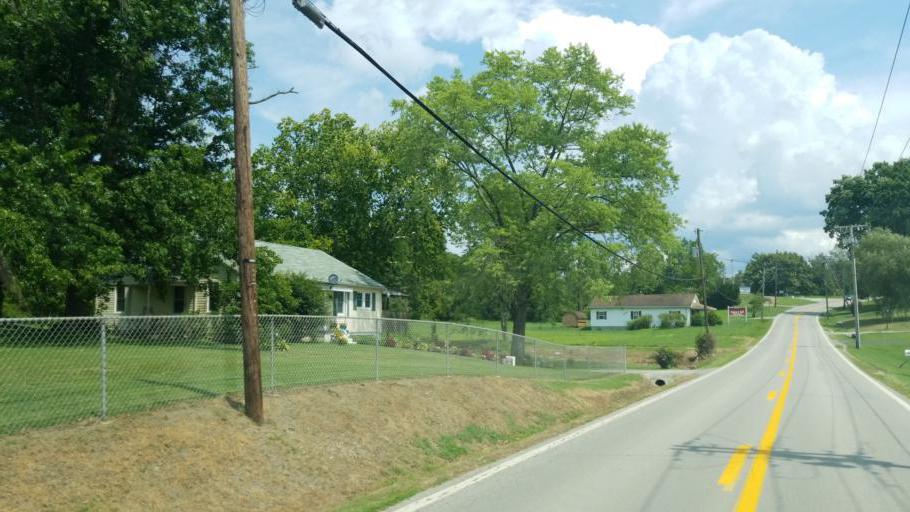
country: US
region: West Virginia
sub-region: Kanawha County
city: Nitro
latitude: 38.4527
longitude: -81.8630
